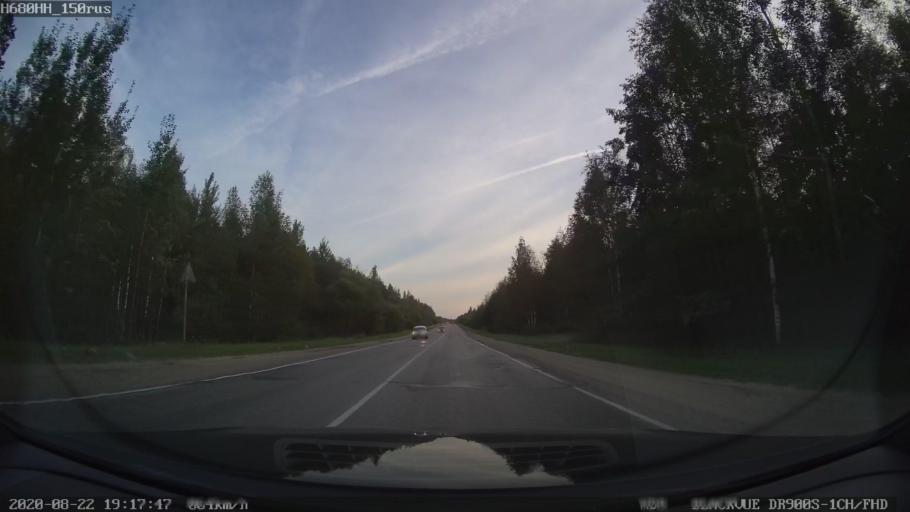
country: RU
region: Tverskaya
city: Sakharovo
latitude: 56.9422
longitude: 36.0094
